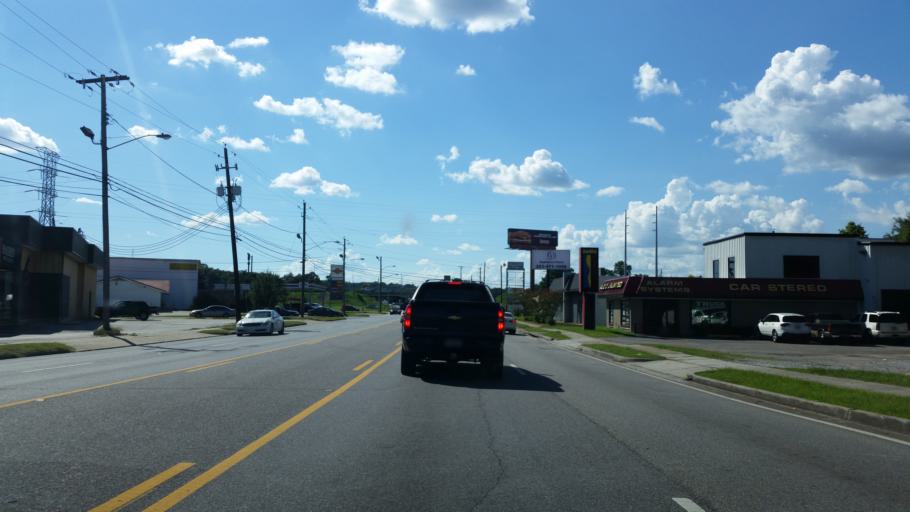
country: US
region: Alabama
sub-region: Mobile County
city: Prichard
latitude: 30.7028
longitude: -88.1198
